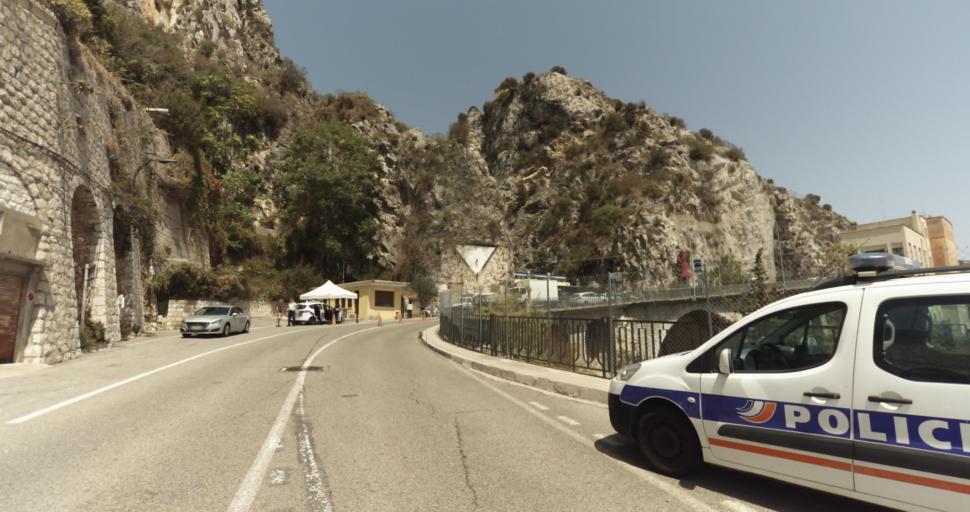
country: FR
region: Provence-Alpes-Cote d'Azur
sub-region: Departement des Alpes-Maritimes
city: Menton
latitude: 43.7861
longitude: 7.5291
